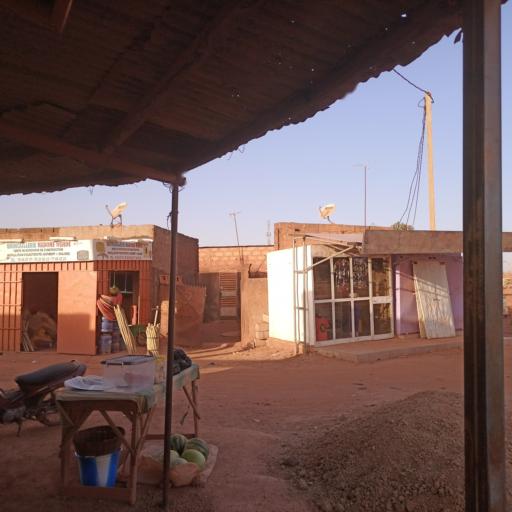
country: BF
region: Centre
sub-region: Kadiogo Province
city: Ouagadougou
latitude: 12.3276
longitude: -1.4778
